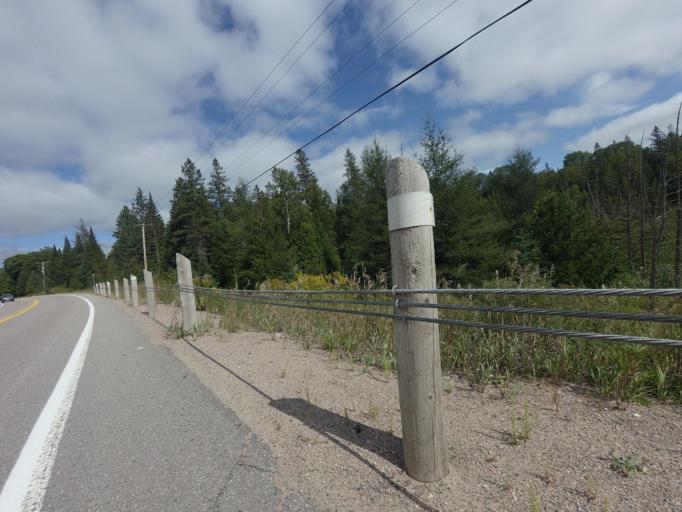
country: CA
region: Ontario
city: Bancroft
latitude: 44.9359
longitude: -78.3041
